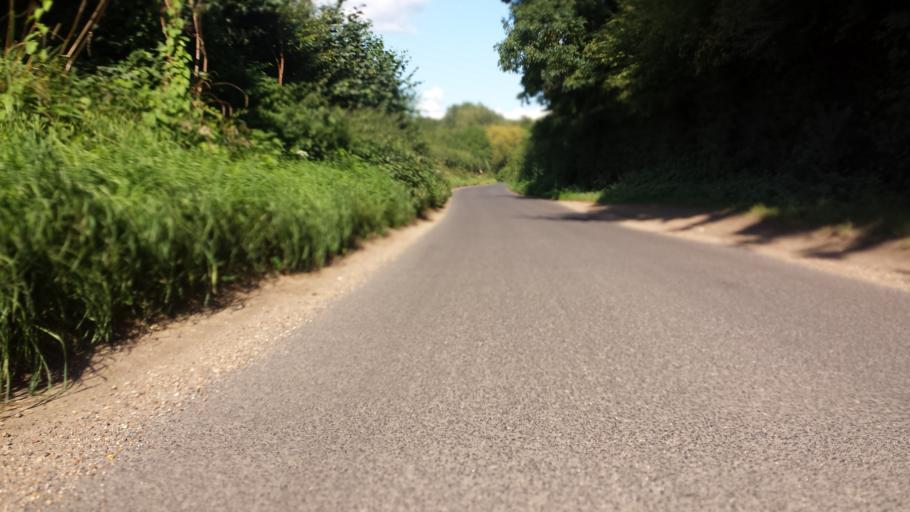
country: GB
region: England
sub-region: Kent
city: Shoreham
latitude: 51.3509
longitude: 0.1883
